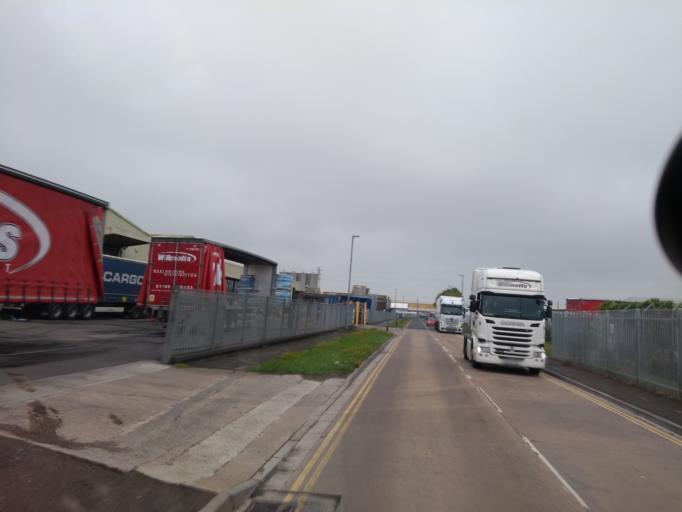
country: GB
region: England
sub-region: Somerset
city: Bridgwater
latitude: 51.1198
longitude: -2.9924
